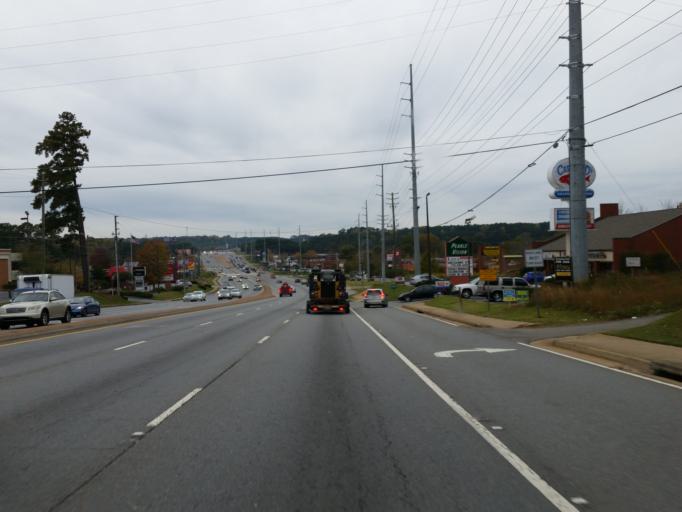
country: US
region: Georgia
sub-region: Cherokee County
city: Woodstock
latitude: 34.0863
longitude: -84.5248
